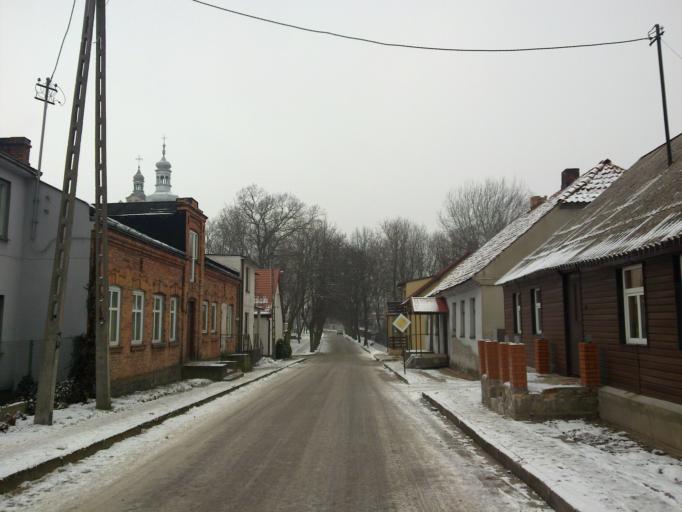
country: PL
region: Kujawsko-Pomorskie
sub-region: Powiat aleksandrowski
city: Raciazek
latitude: 52.8572
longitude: 18.8141
